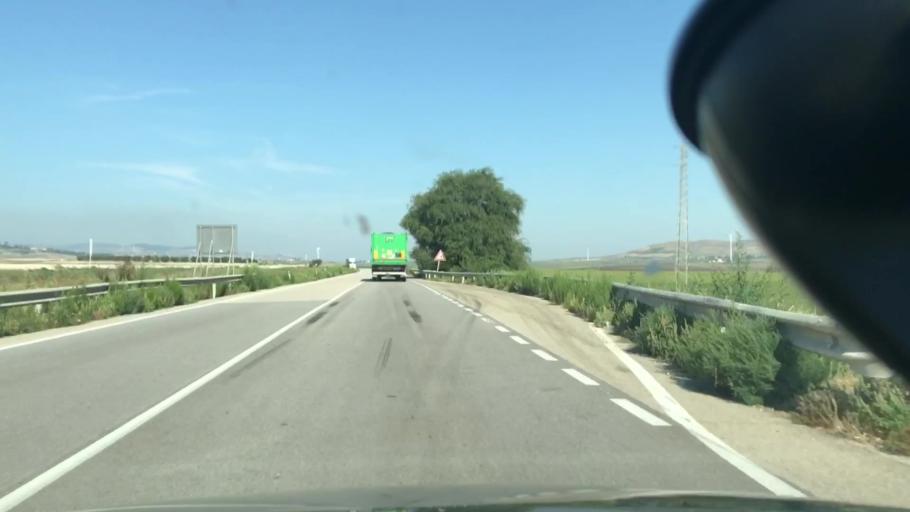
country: IT
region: Apulia
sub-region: Provincia di Foggia
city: Candela
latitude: 41.1147
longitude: 15.5807
